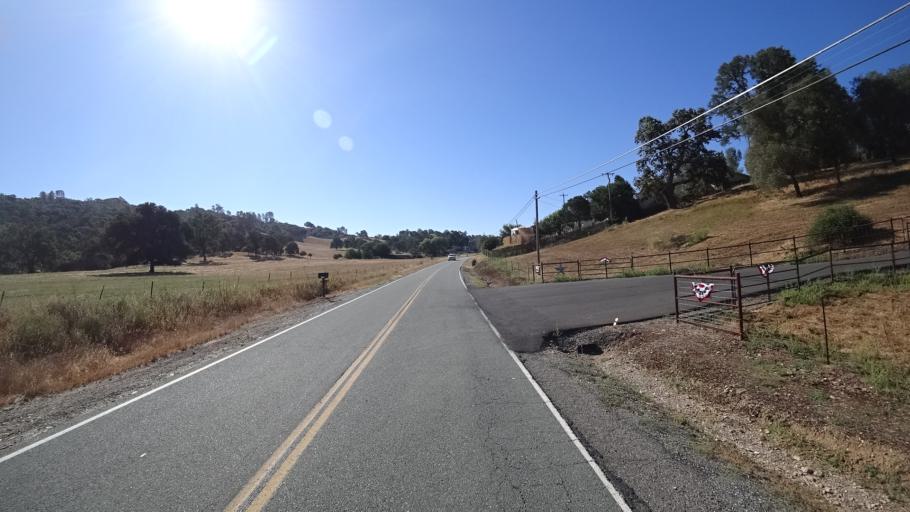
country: US
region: California
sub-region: Calaveras County
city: San Andreas
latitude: 38.2249
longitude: -120.6981
